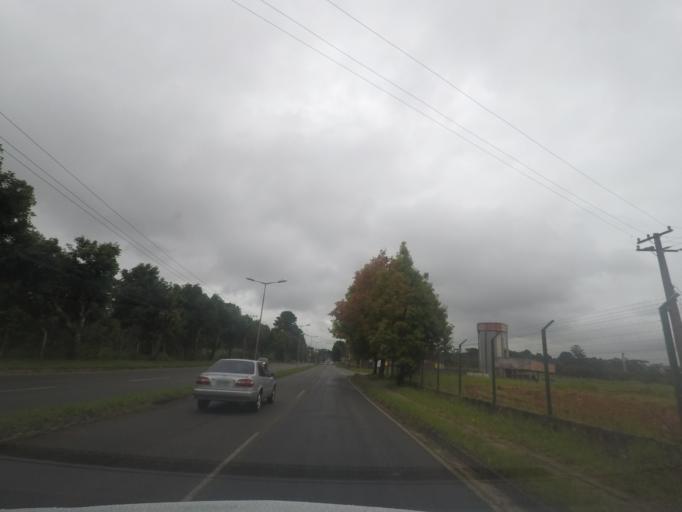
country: BR
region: Parana
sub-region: Pinhais
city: Pinhais
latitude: -25.3931
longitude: -49.1725
